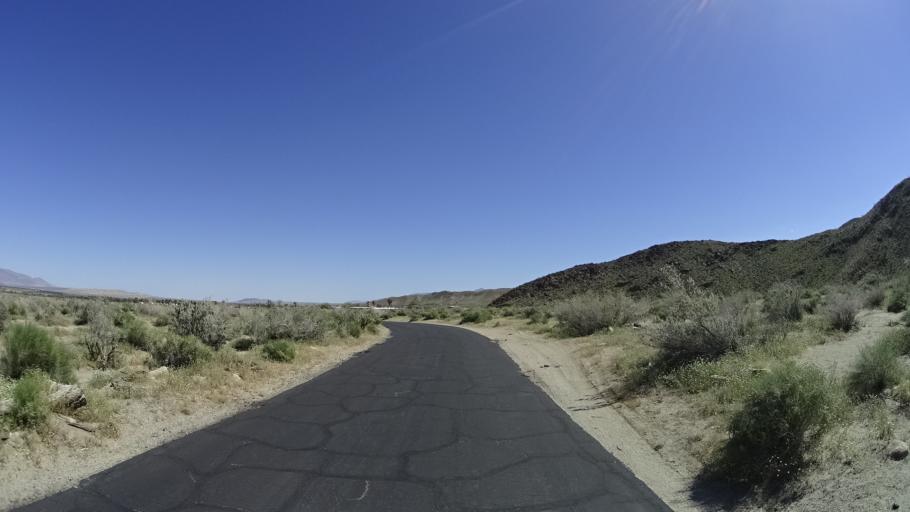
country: US
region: California
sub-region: San Diego County
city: Borrego Springs
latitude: 33.2707
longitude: -116.4159
